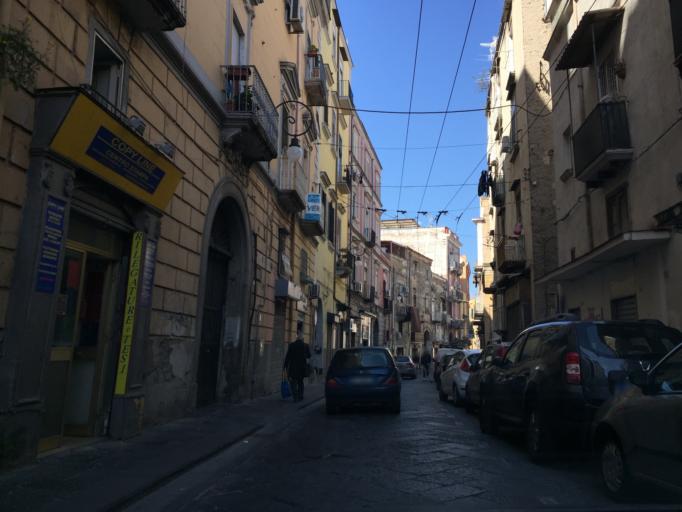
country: IT
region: Campania
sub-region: Provincia di Napoli
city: Portici
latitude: 40.8130
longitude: 14.3402
